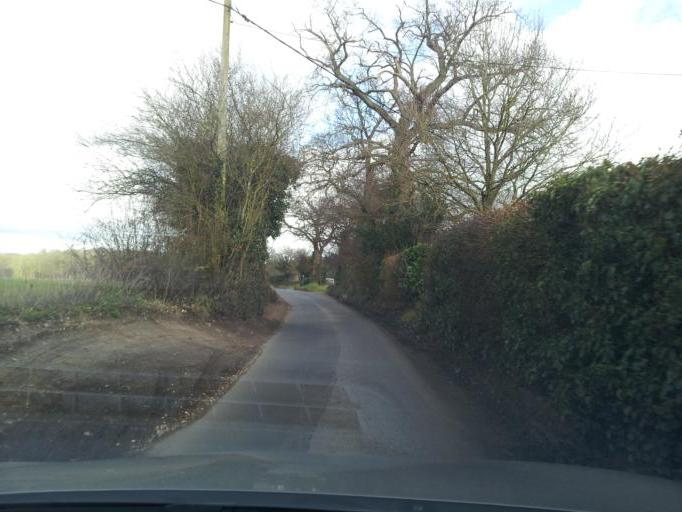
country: GB
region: England
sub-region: Norfolk
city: Costessey
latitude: 52.6998
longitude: 1.1280
